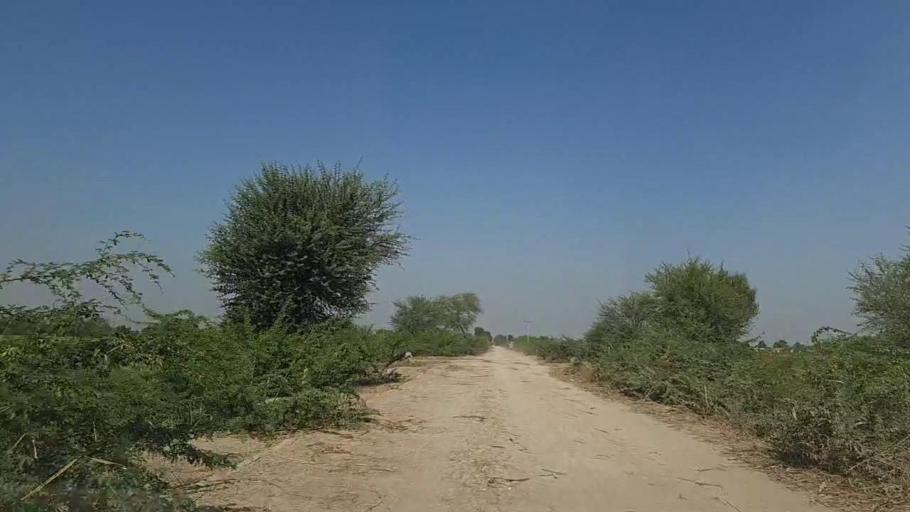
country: PK
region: Sindh
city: Samaro
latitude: 25.1782
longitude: 69.4040
